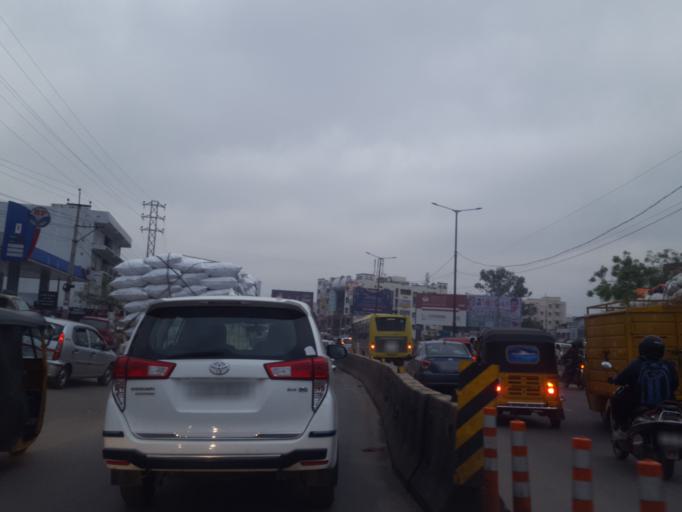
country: IN
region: Telangana
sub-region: Medak
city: Serilingampalle
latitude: 17.4958
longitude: 78.3159
